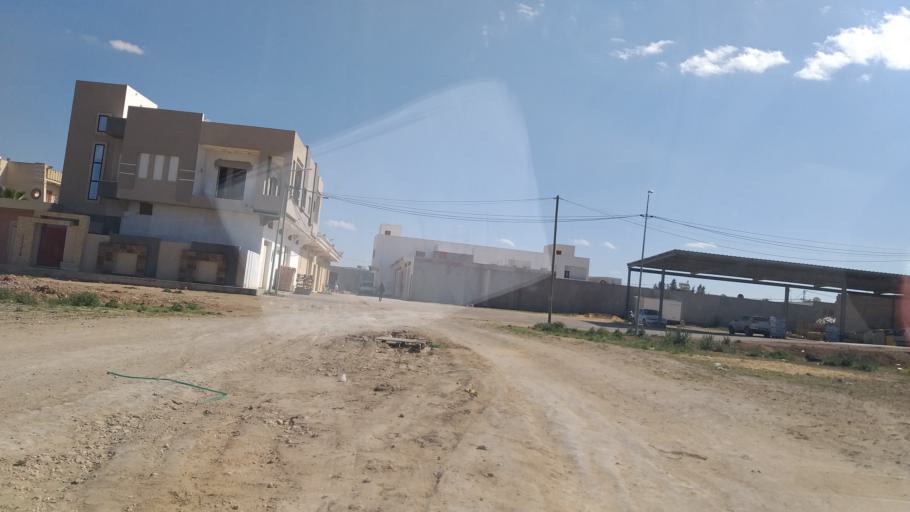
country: TN
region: Al Mahdiyah
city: El Jem
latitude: 35.2950
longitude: 10.6940
